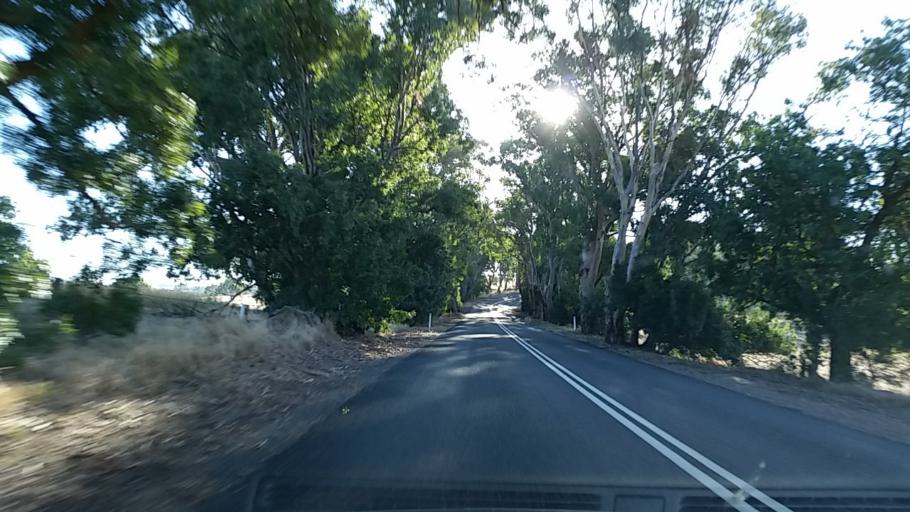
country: AU
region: South Australia
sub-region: Adelaide Hills
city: Birdwood
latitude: -34.7741
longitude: 139.0804
